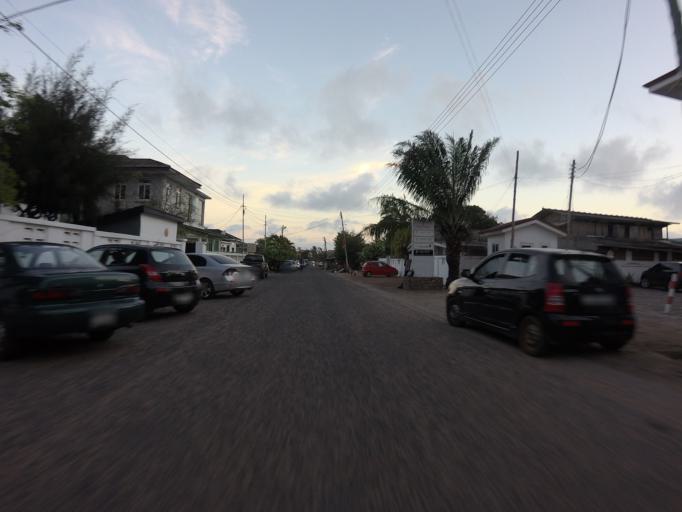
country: GH
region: Greater Accra
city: Accra
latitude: 5.5579
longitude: -0.1726
